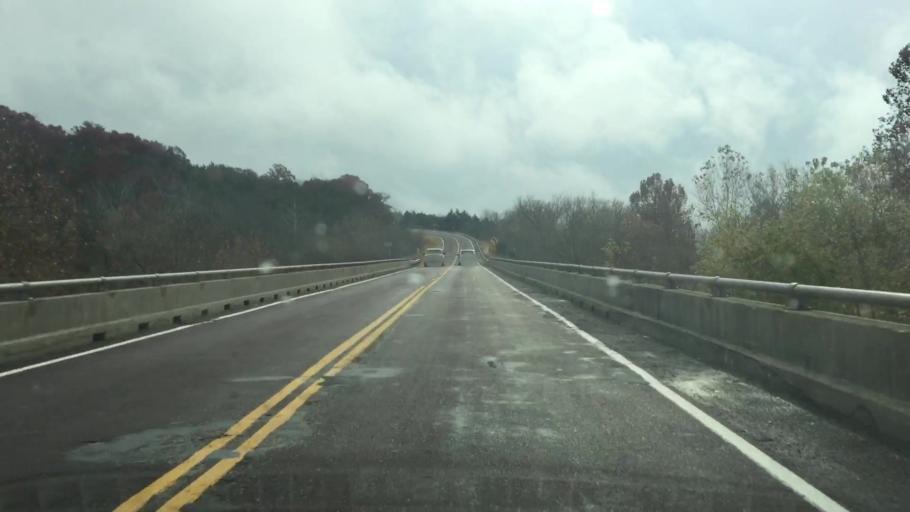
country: US
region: Missouri
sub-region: Callaway County
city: Fulton
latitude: 38.7801
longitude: -91.8506
